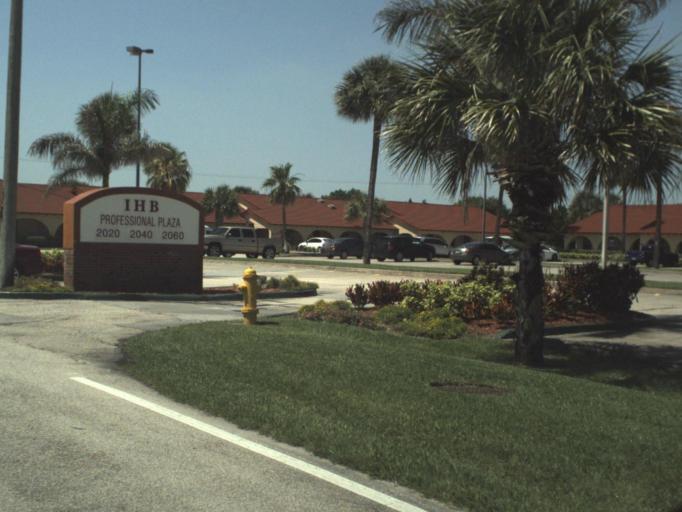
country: US
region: Florida
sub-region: Brevard County
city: Indian Harbour Beach
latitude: 28.1475
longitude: -80.5833
